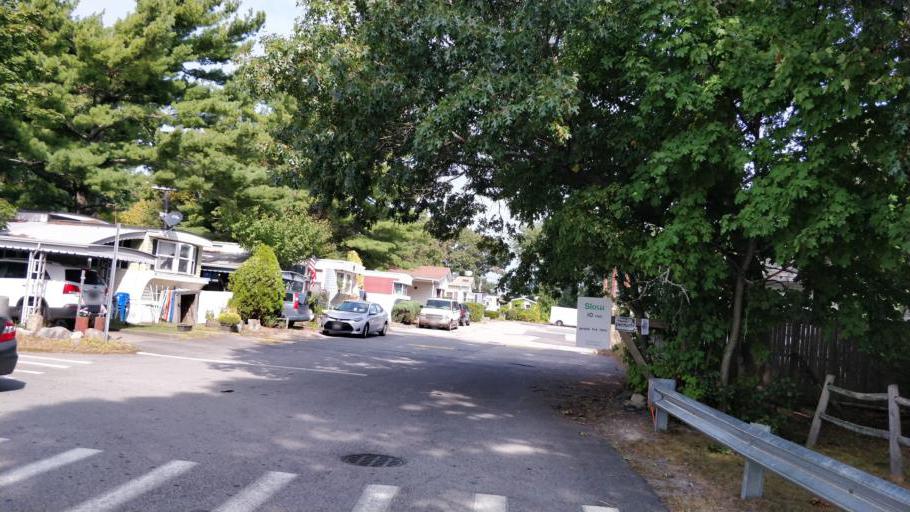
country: US
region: Massachusetts
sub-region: Bristol County
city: North Seekonk
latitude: 41.8970
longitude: -71.3511
